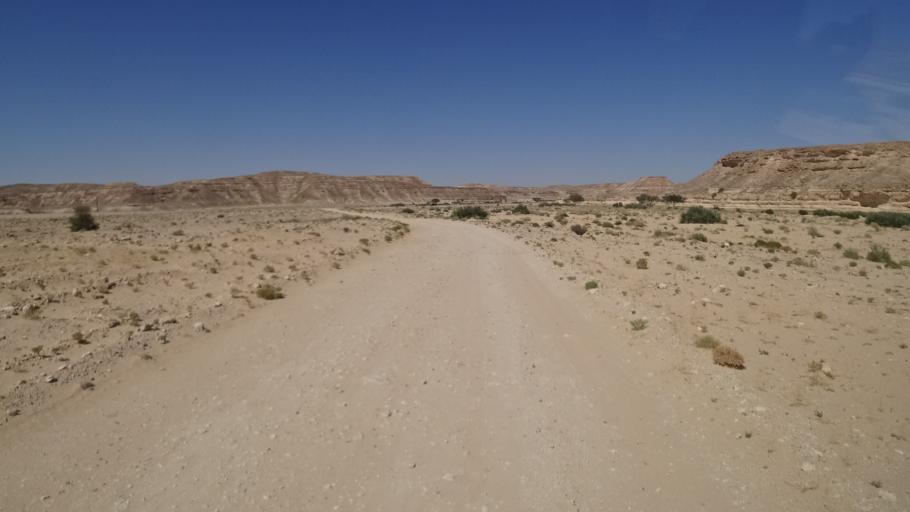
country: OM
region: Zufar
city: Salalah
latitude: 17.5019
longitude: 53.3648
